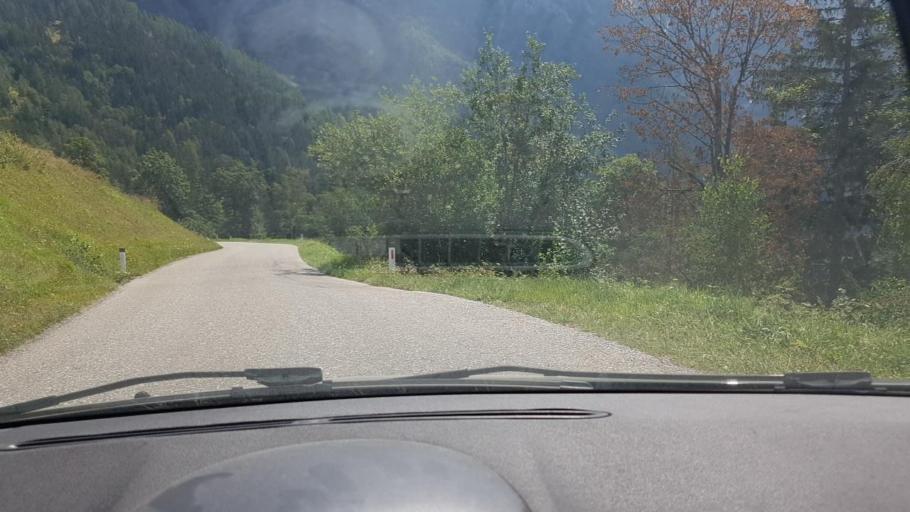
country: SI
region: Jezersko
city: Zgornje Jezersko
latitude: 46.4150
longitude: 14.5640
